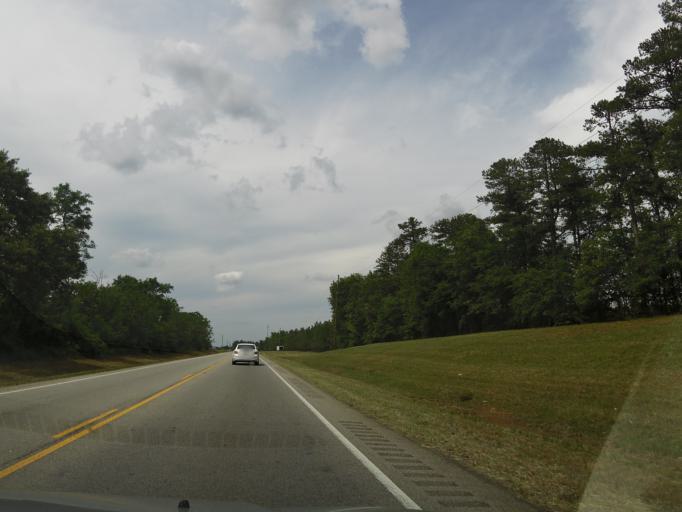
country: US
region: Georgia
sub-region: Jefferson County
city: Louisville
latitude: 33.0740
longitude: -82.4051
